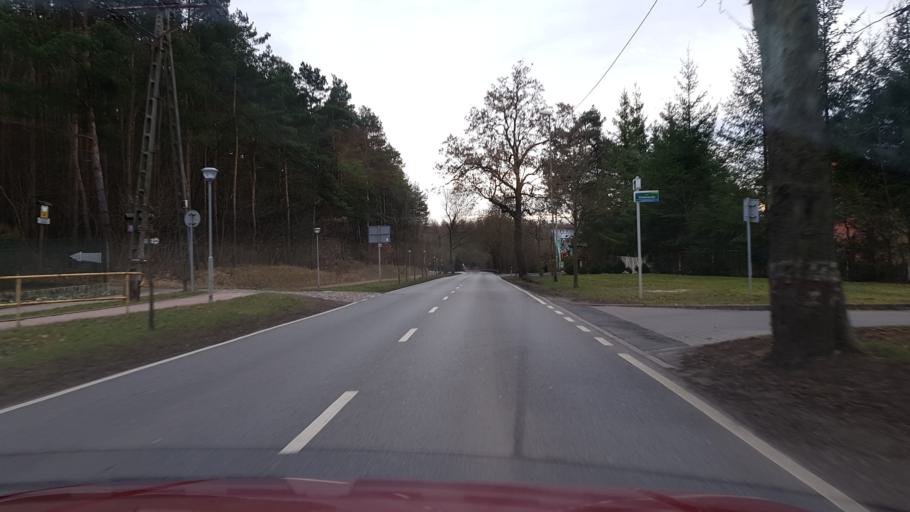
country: PL
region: West Pomeranian Voivodeship
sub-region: Powiat policki
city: Dobra
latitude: 53.4917
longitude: 14.4810
